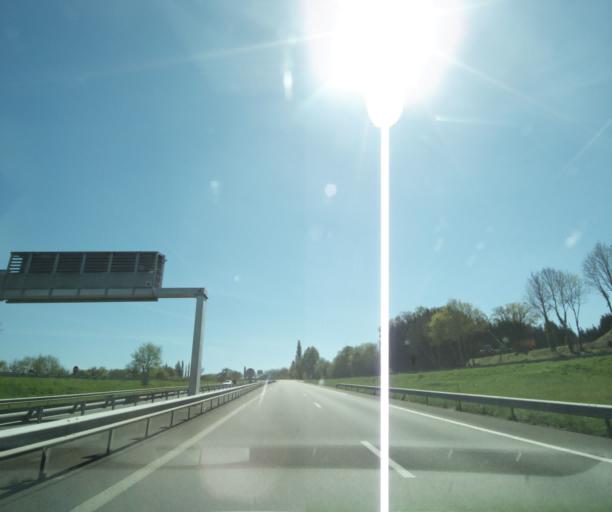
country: FR
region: Limousin
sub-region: Departement de la Haute-Vienne
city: Pierre-Buffiere
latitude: 45.6868
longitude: 1.3669
